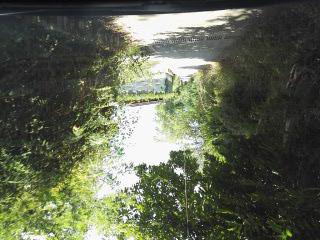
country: IT
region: Calabria
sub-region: Provincia di Vibo-Valentia
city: Serra San Bruno
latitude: 38.5604
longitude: 16.3311
